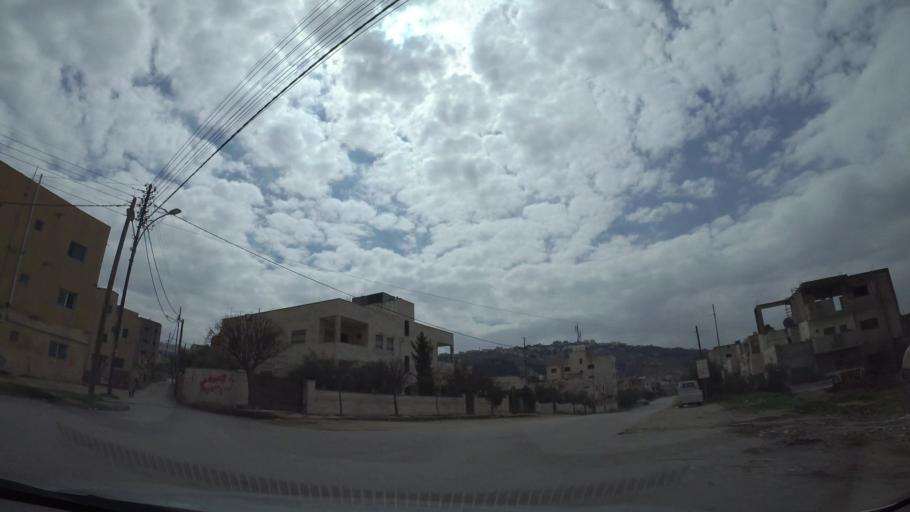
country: JO
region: Amman
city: Al Jubayhah
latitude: 32.0517
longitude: 35.8283
